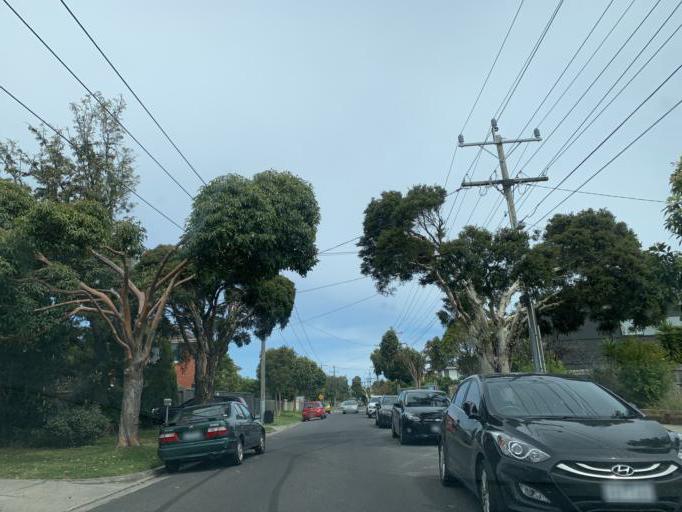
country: AU
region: Victoria
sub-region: Bayside
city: Hampton East
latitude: -37.9338
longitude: 145.0285
